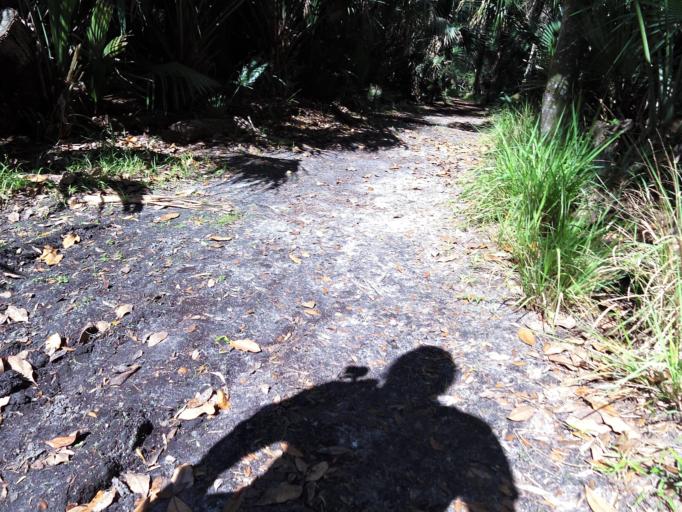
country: US
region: Florida
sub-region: Flagler County
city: Flagler Beach
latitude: 29.4273
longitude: -81.1425
